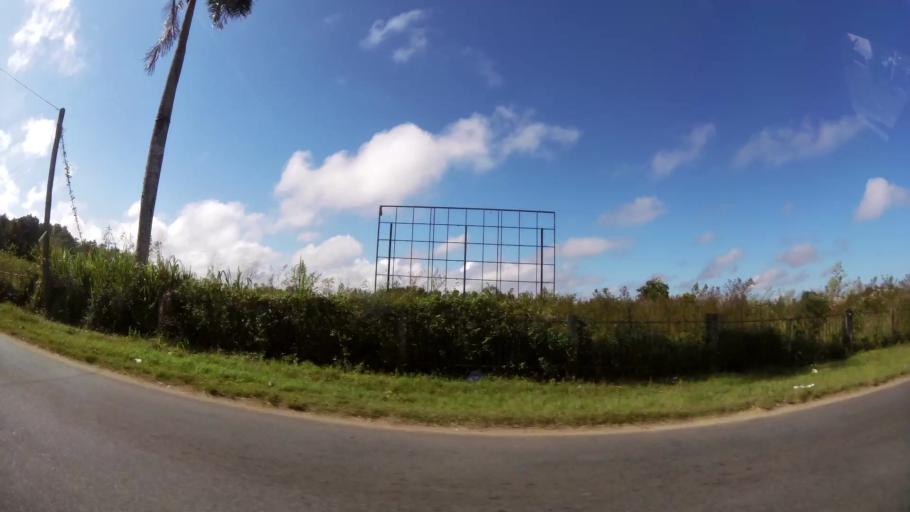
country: SR
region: Paramaribo
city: Paramaribo
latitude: 5.8320
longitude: -55.1377
